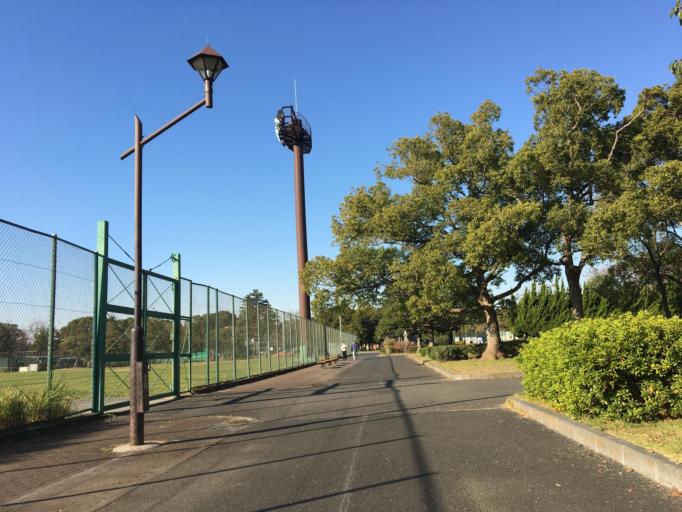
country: JP
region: Tokyo
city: Urayasu
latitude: 35.7149
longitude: 139.8993
